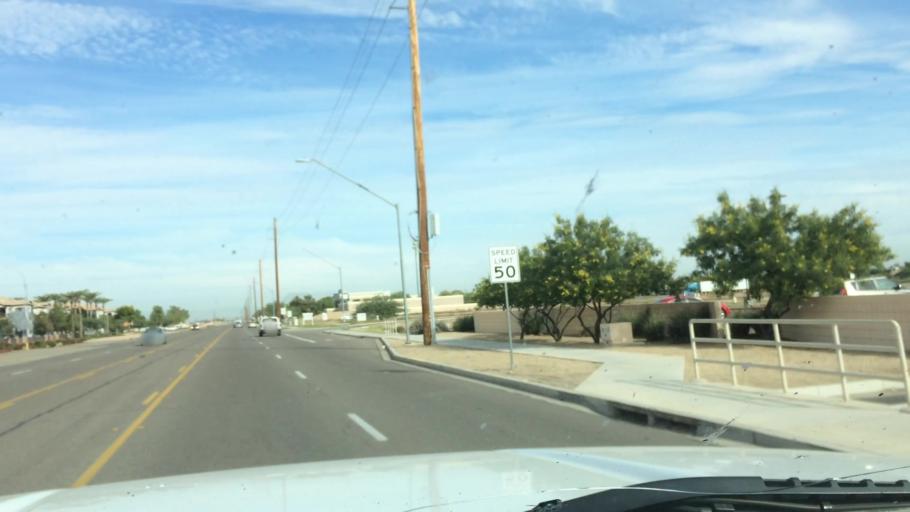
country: US
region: Arizona
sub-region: Maricopa County
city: Tolleson
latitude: 33.5092
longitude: -112.2725
